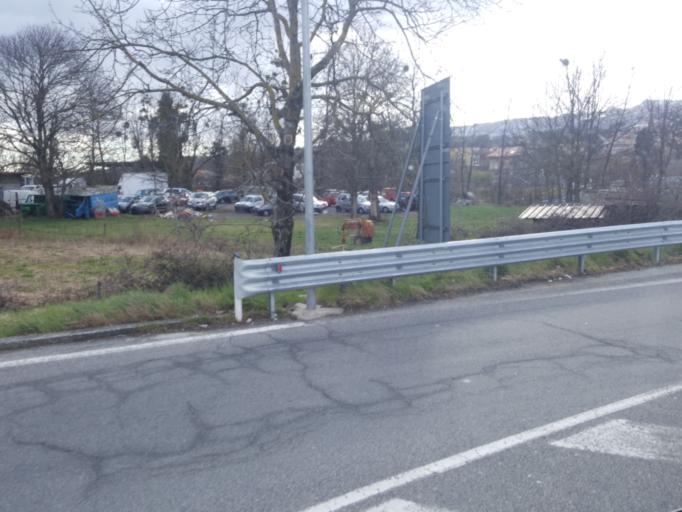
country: IT
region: Calabria
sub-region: Provincia di Cosenza
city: Santo Stefano di Rogliano
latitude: 39.1993
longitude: 16.3137
